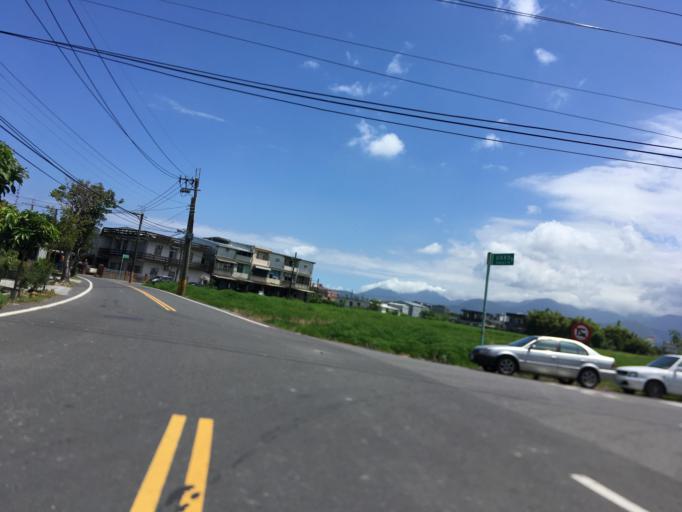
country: TW
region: Taiwan
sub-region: Yilan
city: Yilan
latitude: 24.6851
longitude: 121.8021
